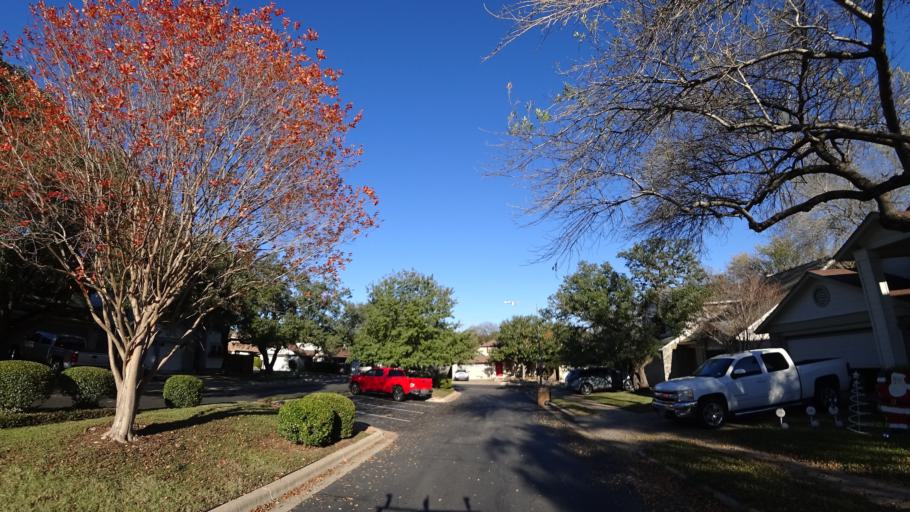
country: US
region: Texas
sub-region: Travis County
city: Wells Branch
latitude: 30.3975
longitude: -97.6907
